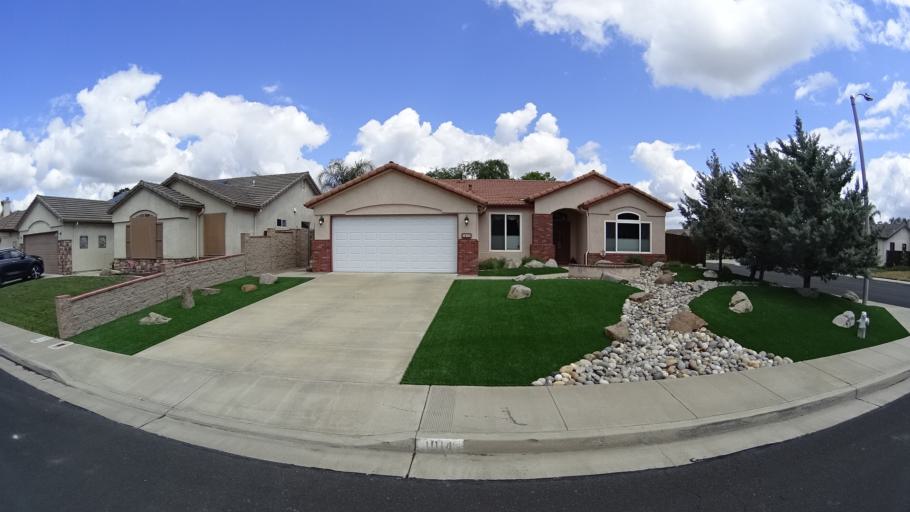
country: US
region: California
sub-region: Kings County
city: Lucerne
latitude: 36.3617
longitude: -119.6605
